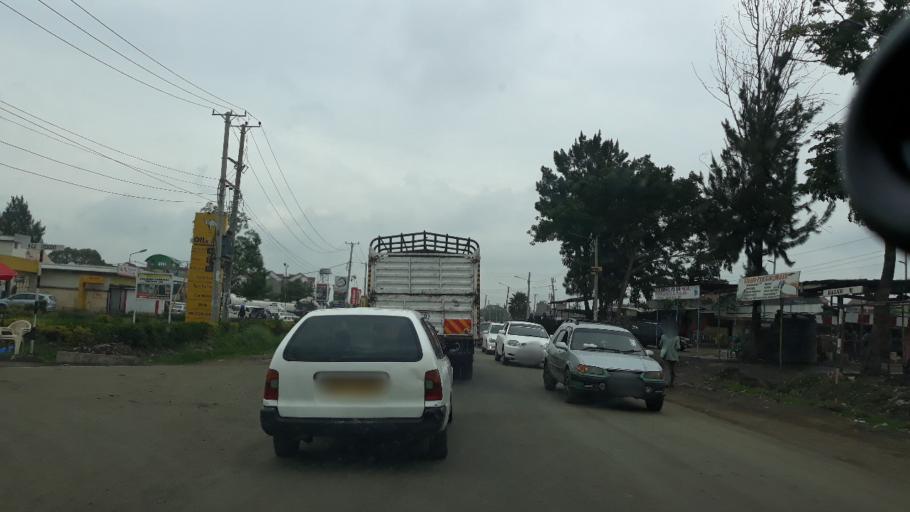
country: KE
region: Nairobi Area
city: Pumwani
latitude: -1.2757
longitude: 36.8884
